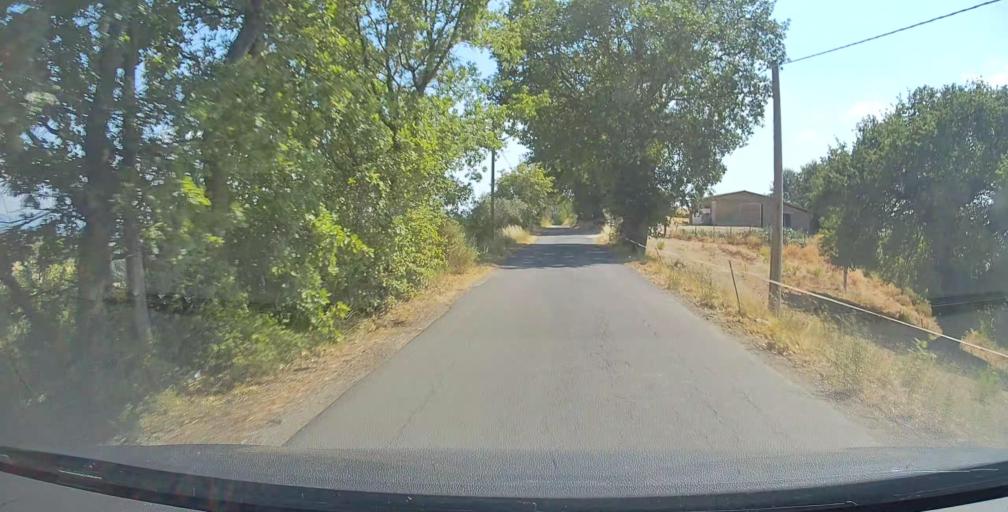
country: IT
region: Umbria
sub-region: Provincia di Terni
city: Calvi dell'Umbria
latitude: 42.3802
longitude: 12.5686
